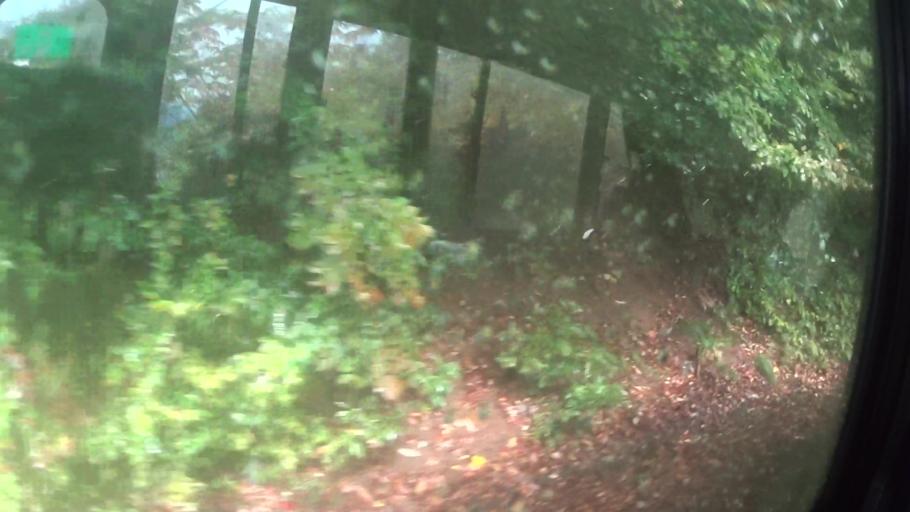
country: JP
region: Kyoto
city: Miyazu
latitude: 35.5857
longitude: 135.1937
